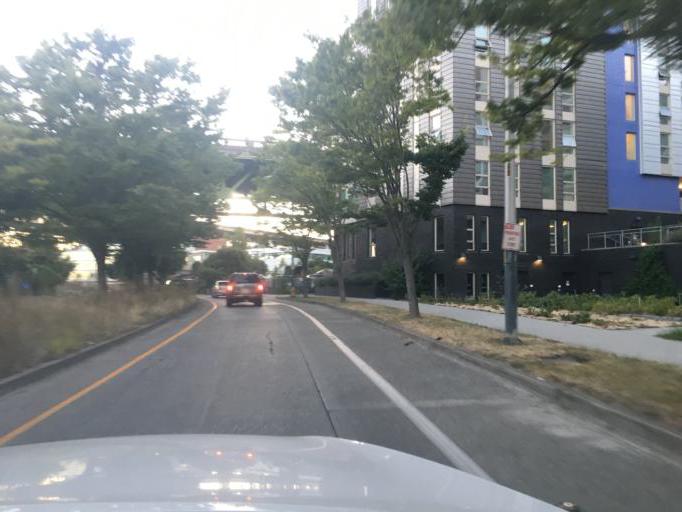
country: US
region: Washington
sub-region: King County
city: Seattle
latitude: 47.6541
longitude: -122.3182
